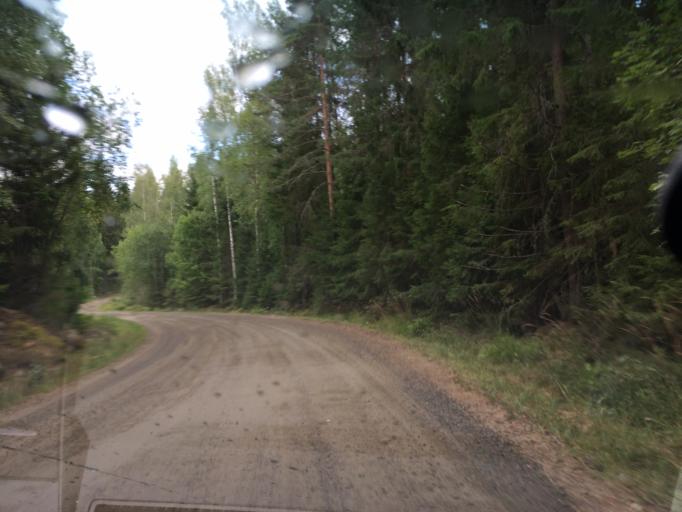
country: FI
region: Pirkanmaa
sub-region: Tampere
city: Luopioinen
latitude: 61.2715
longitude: 24.6751
